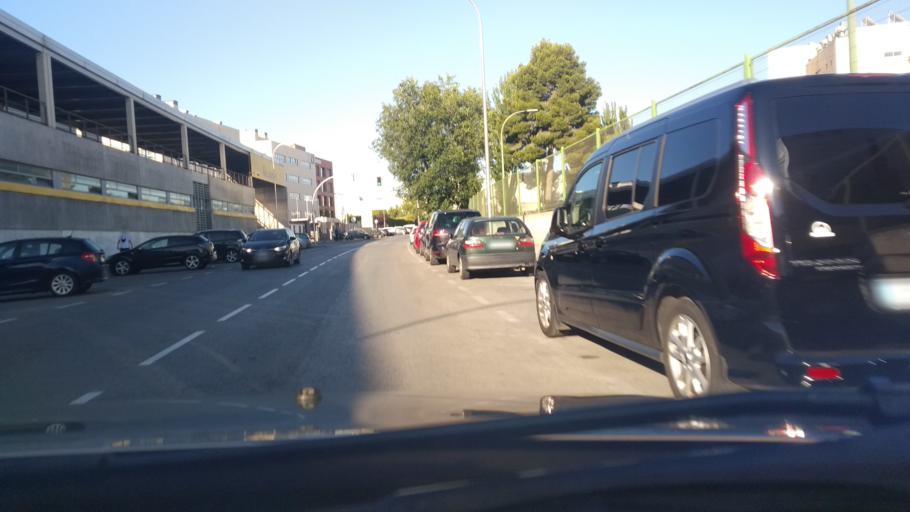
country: ES
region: Madrid
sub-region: Provincia de Madrid
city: Puente de Vallecas
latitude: 40.3768
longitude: -3.6356
